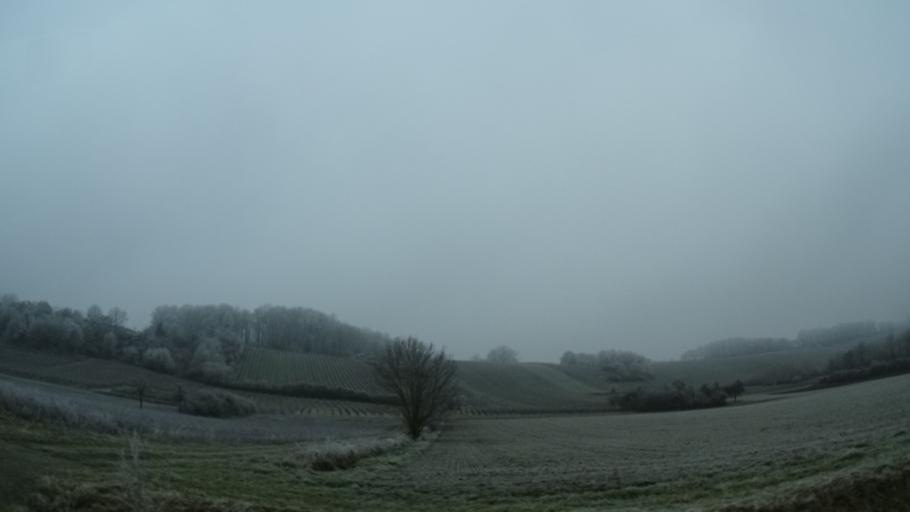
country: DE
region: Bavaria
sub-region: Regierungsbezirk Unterfranken
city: Marktsteft
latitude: 49.6960
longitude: 10.1246
